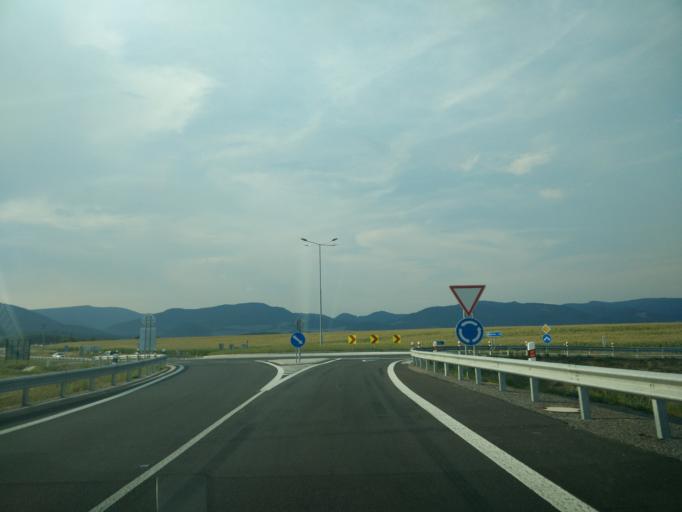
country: SK
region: Banskobystricky
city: Ziar nad Hronom
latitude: 48.6198
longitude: 18.8016
